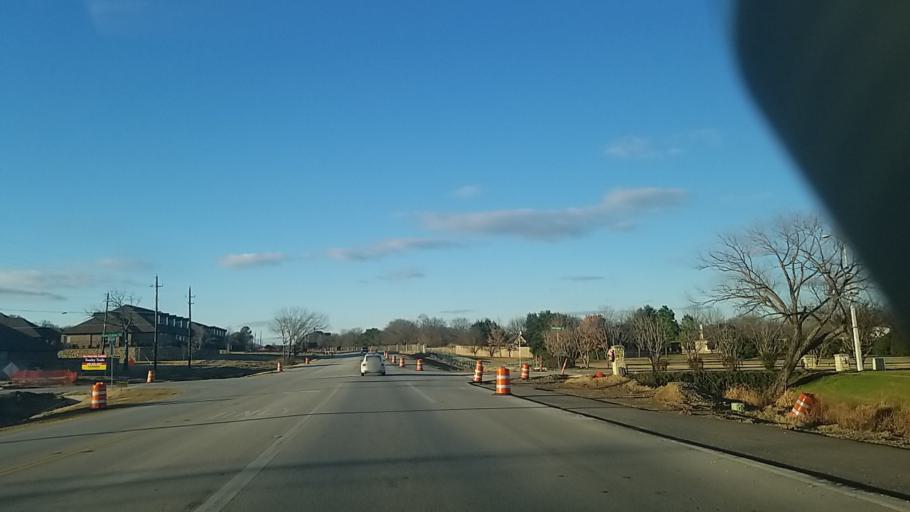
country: US
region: Texas
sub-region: Denton County
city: Corinth
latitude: 33.1658
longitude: -97.1092
